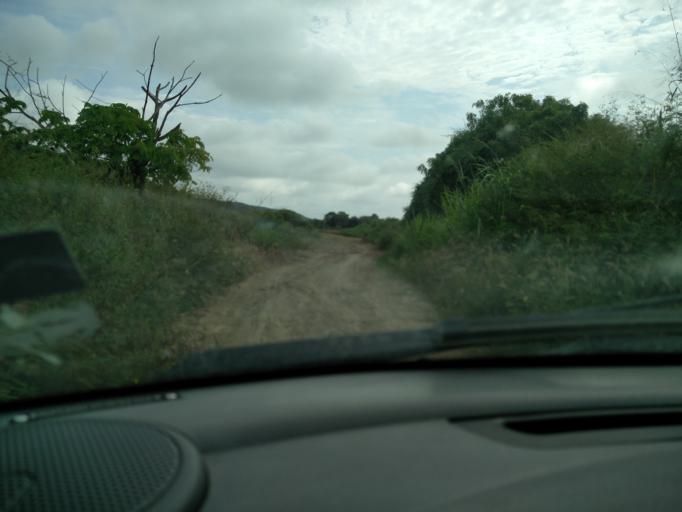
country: EC
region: Manabi
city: Rocafuerte
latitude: -0.8637
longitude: -80.5183
